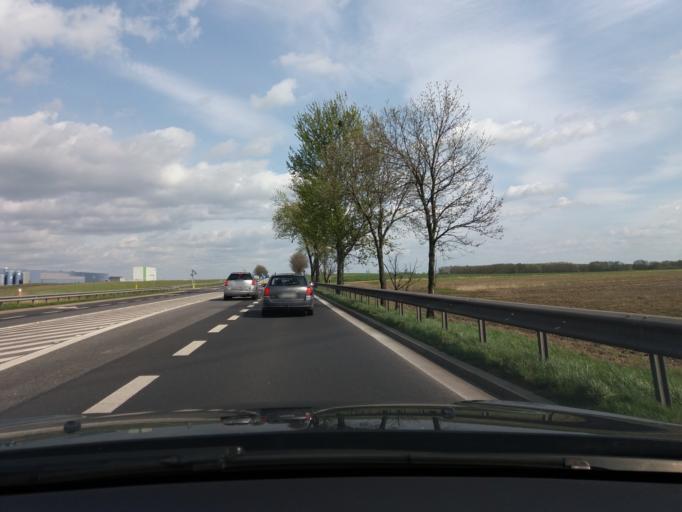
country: PL
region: Lower Silesian Voivodeship
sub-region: Powiat sredzki
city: Szczepanow
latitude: 51.1646
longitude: 16.6454
